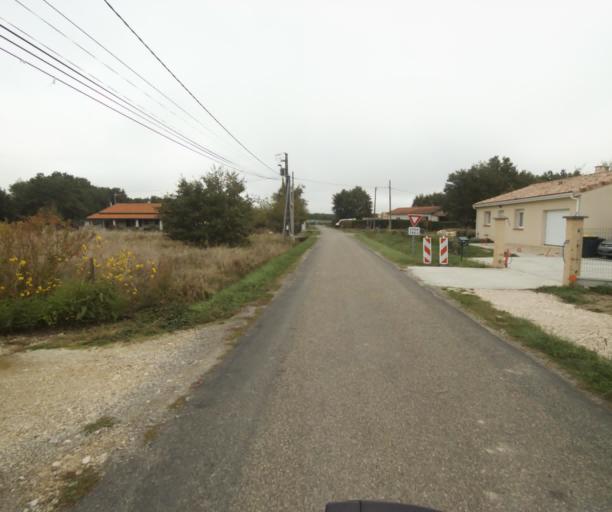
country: FR
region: Midi-Pyrenees
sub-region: Departement du Tarn-et-Garonne
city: Labastide-Saint-Pierre
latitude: 43.8853
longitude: 1.3786
